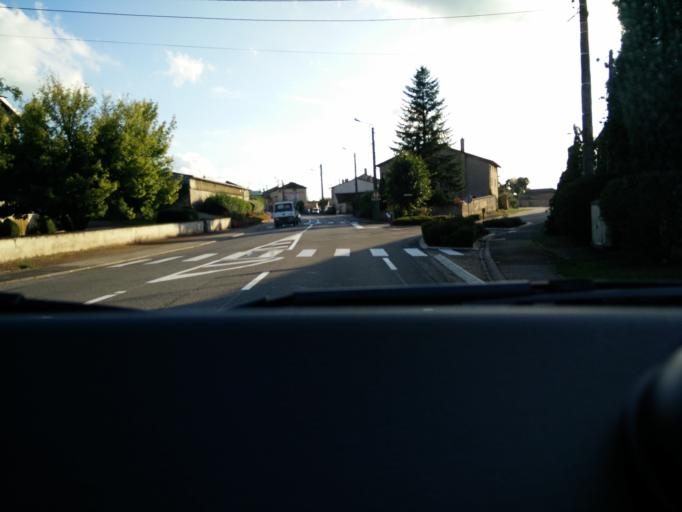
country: FR
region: Lorraine
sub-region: Departement de Meurthe-et-Moselle
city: Luneville
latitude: 48.5636
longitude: 6.4712
